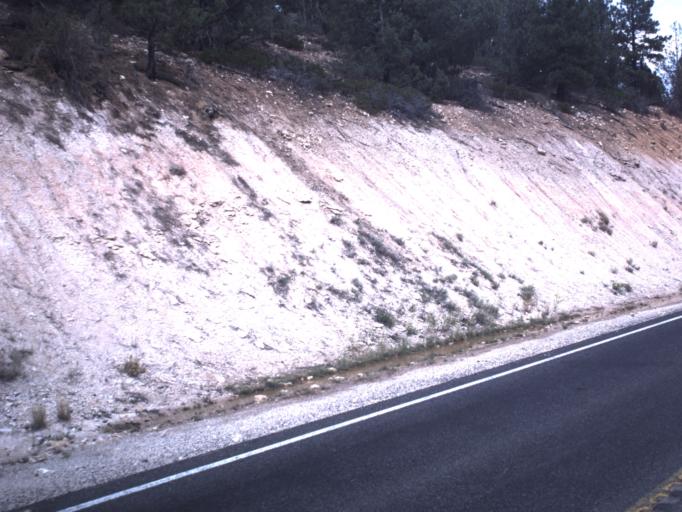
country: US
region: Utah
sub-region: Kane County
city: Kanab
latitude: 37.4411
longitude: -112.5379
